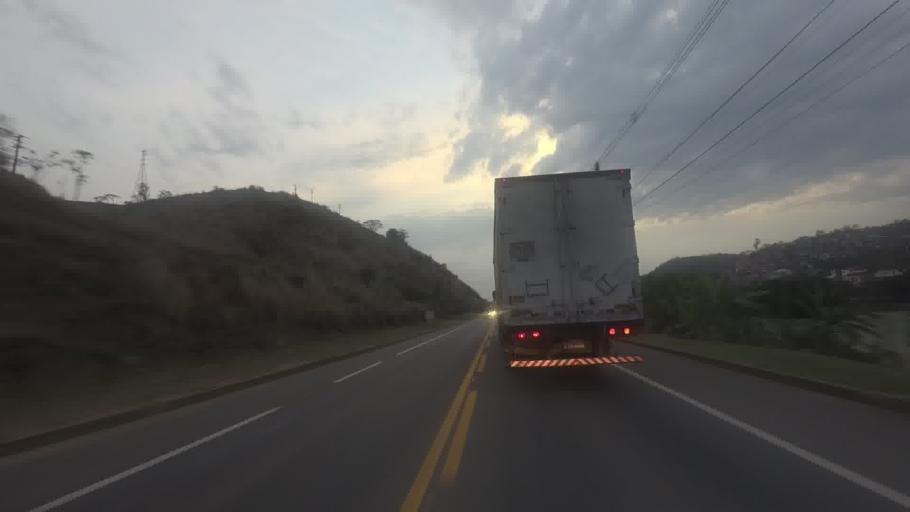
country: BR
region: Minas Gerais
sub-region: Alem Paraiba
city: Alem Paraiba
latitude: -21.8845
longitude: -42.6923
